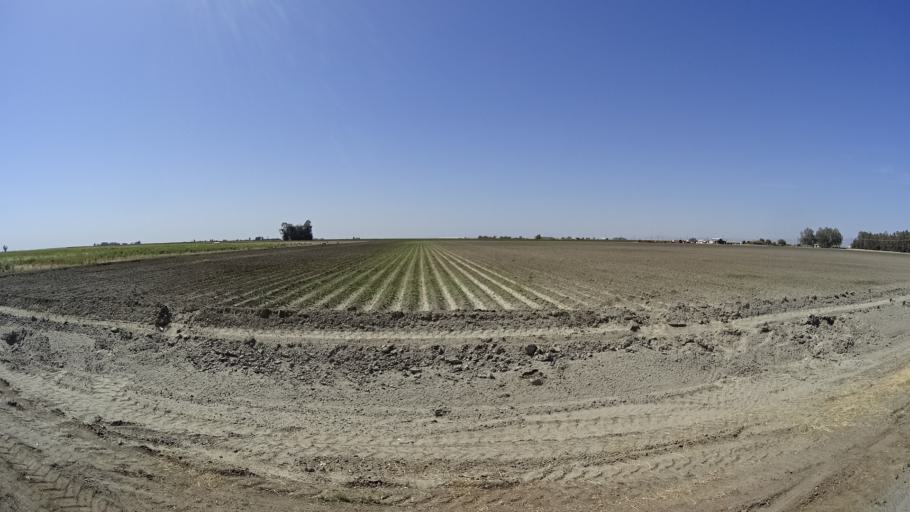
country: US
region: California
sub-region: Kings County
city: Stratford
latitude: 36.1967
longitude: -119.7939
